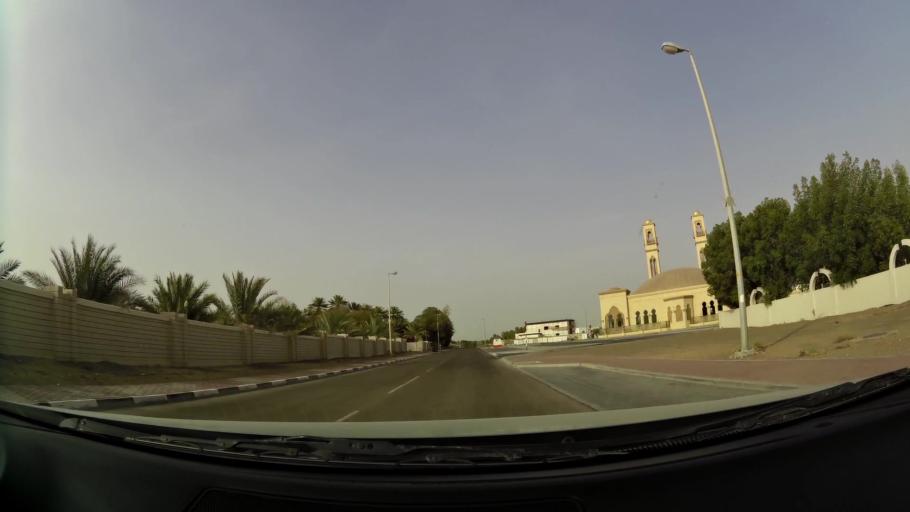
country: AE
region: Abu Dhabi
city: Al Ain
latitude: 24.2173
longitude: 55.6698
